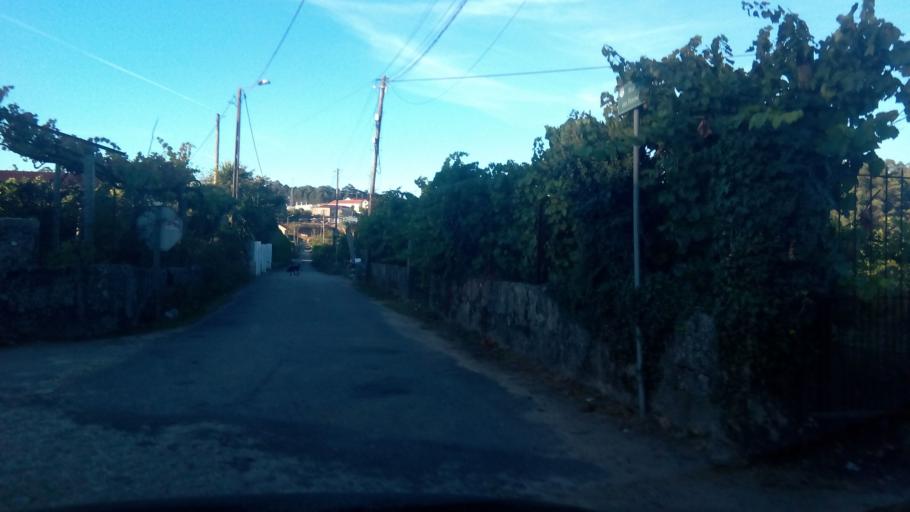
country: PT
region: Porto
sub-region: Paredes
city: Baltar
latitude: 41.1823
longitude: -8.3813
